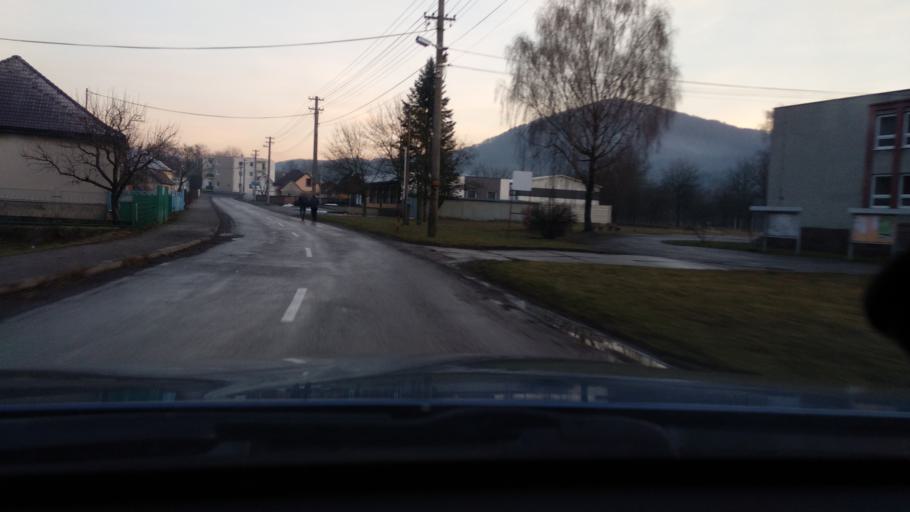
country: SK
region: Nitriansky
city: Banovce nad Bebravou
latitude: 48.8379
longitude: 18.2613
